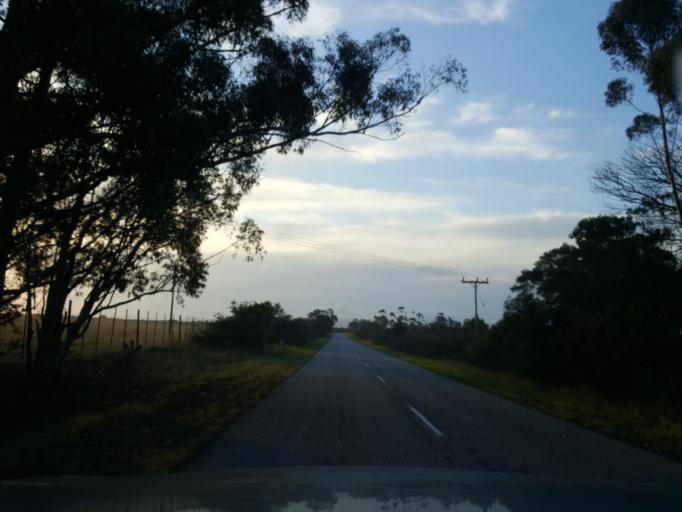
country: ZA
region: Eastern Cape
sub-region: Cacadu District Municipality
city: Grahamstown
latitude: -33.4452
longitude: 26.4853
